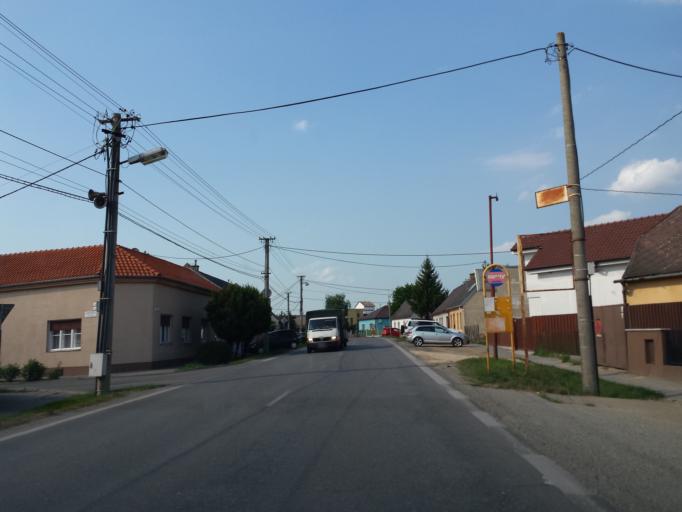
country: SK
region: Bratislavsky
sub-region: Okres Malacky
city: Malacky
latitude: 48.4272
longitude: 17.0209
